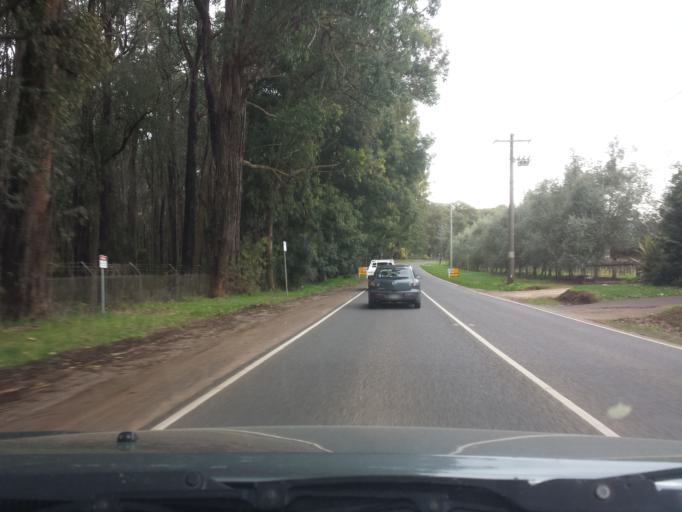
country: AU
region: Victoria
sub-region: Yarra Ranges
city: Monbulk
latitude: -37.8438
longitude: 145.4242
